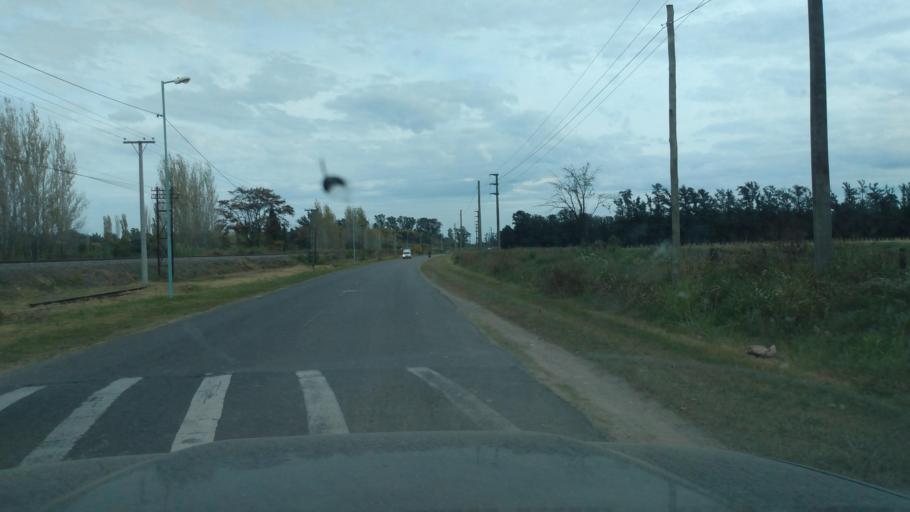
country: AR
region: Buenos Aires
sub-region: Partido de Lujan
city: Lujan
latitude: -34.5933
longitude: -59.1500
